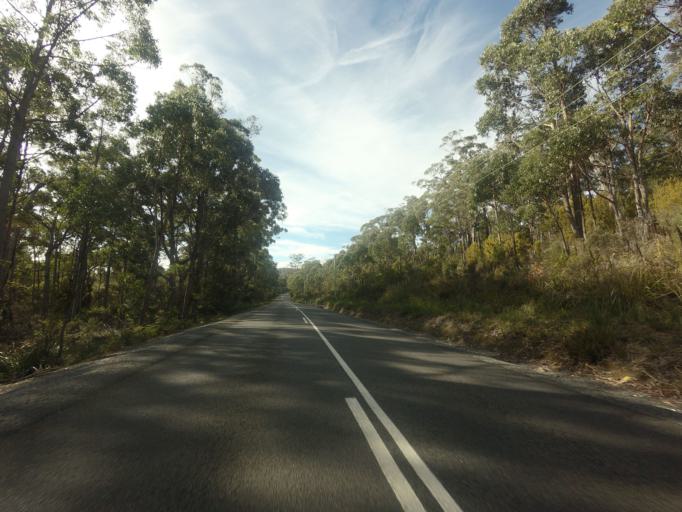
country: AU
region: Tasmania
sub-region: Clarence
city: Sandford
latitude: -43.0620
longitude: 147.8430
